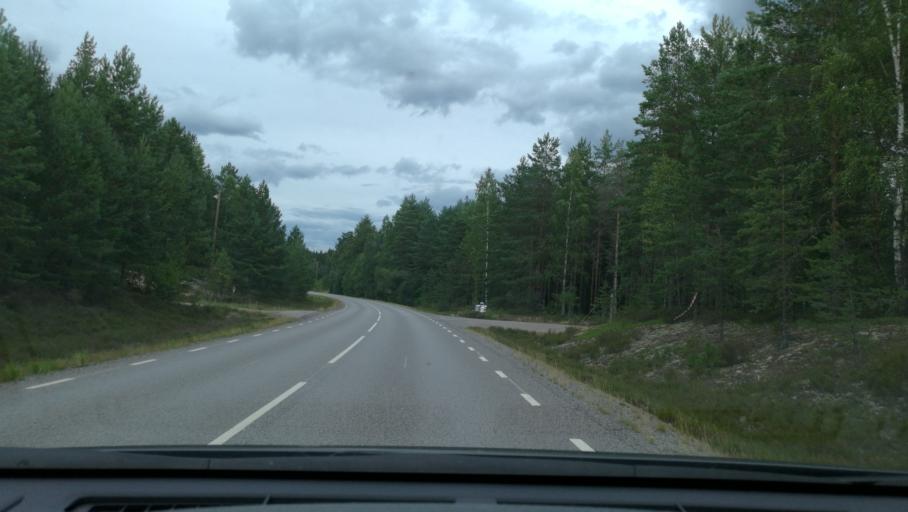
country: SE
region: OEstergoetland
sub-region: Norrkopings Kommun
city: Svartinge
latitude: 58.7503
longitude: 15.9780
